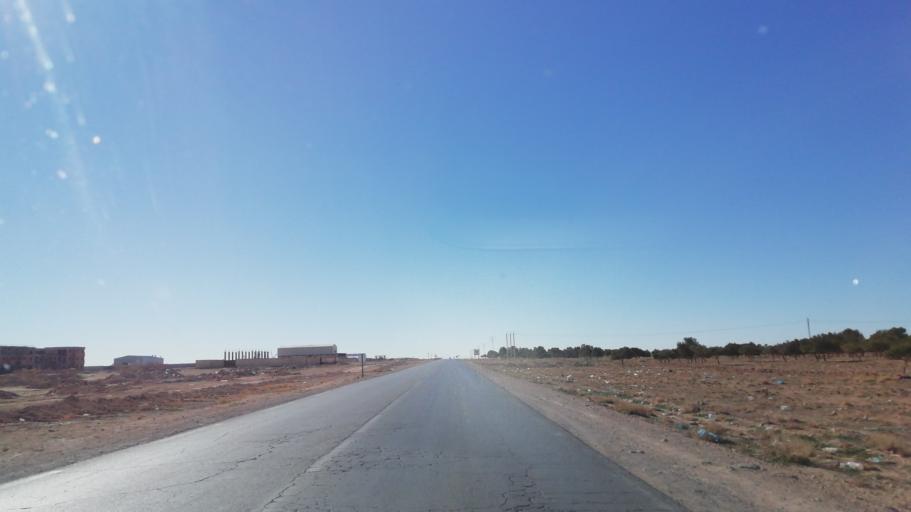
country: DZ
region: Saida
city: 'Ain el Hadjar
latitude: 34.0334
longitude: 0.0756
